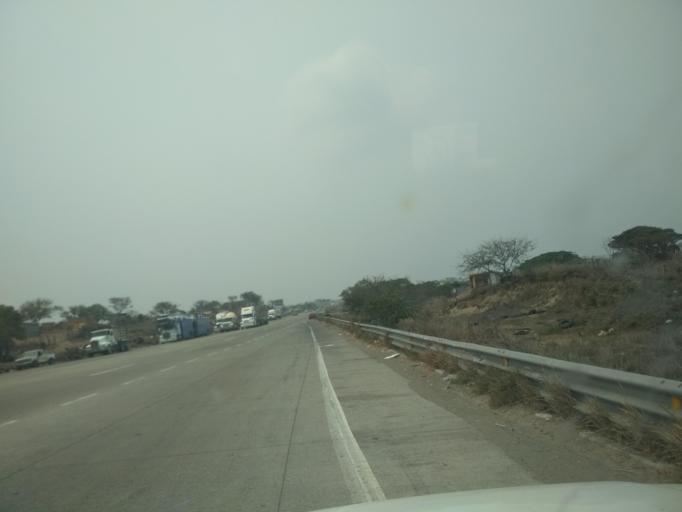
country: MX
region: Veracruz
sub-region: Veracruz
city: Colonia el Renacimiento
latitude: 19.2163
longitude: -96.2209
